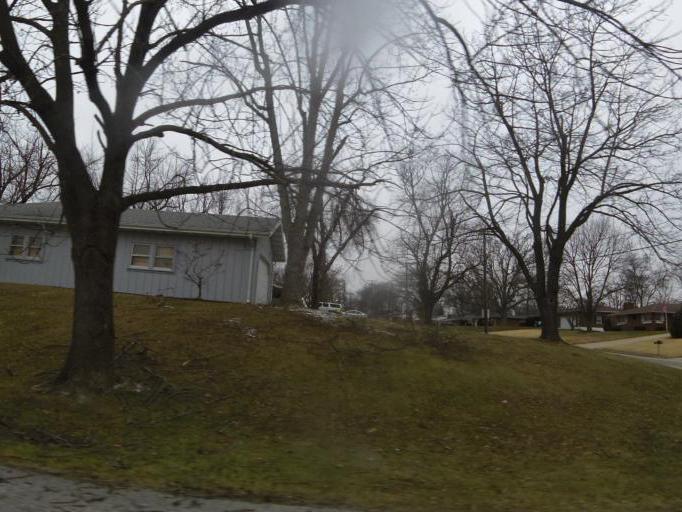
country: US
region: Missouri
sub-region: Marion County
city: Hannibal
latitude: 39.7127
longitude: -91.4021
